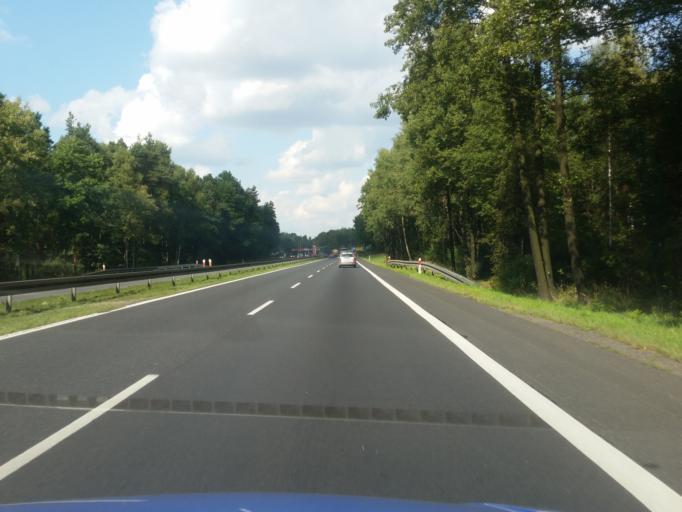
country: PL
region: Silesian Voivodeship
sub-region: Powiat czestochowski
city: Kamienica Polska
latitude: 50.6571
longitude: 19.1310
